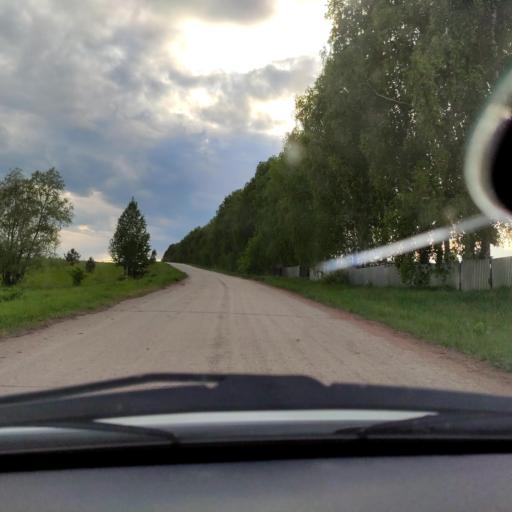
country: RU
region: Bashkortostan
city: Dyurtyuli
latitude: 55.5920
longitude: 54.9504
